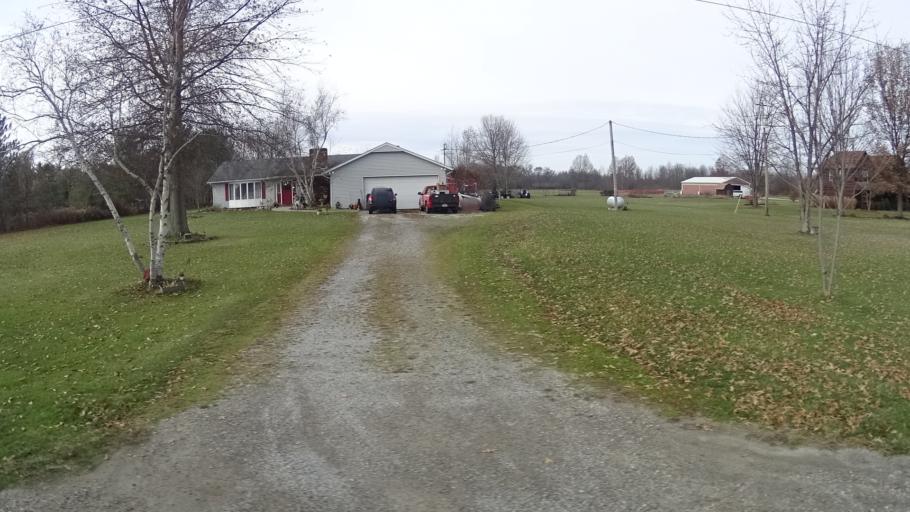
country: US
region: Ohio
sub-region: Lorain County
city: Eaton Estates
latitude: 41.2541
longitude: -82.0028
